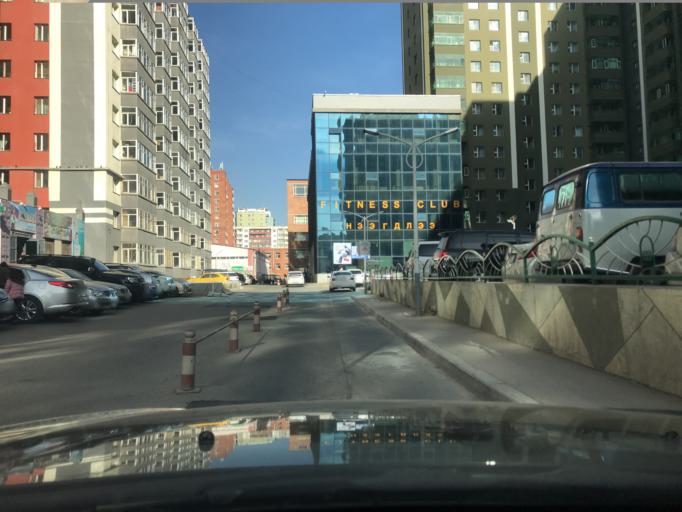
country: MN
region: Ulaanbaatar
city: Ulaanbaatar
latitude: 47.9095
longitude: 106.9416
